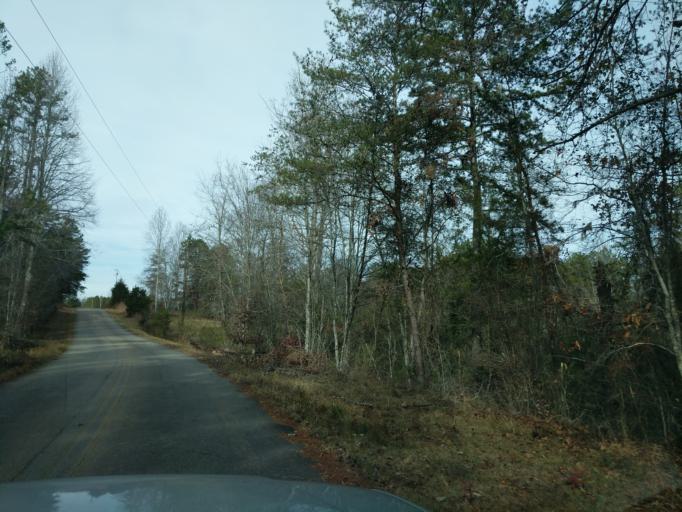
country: US
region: South Carolina
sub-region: Oconee County
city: Walhalla
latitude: 34.8528
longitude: -83.0527
